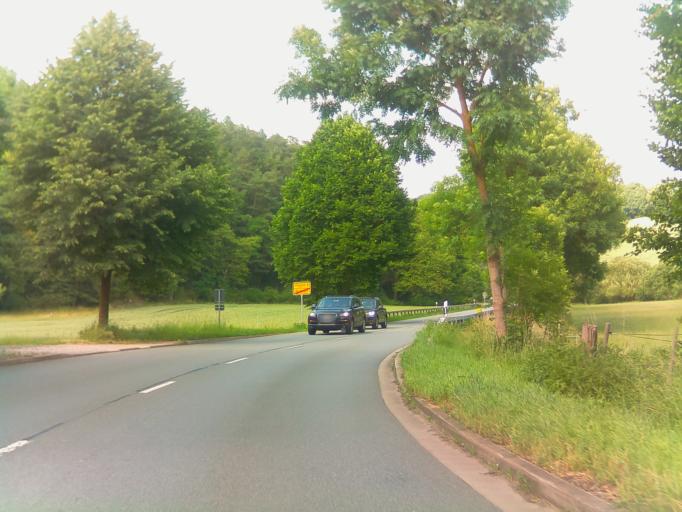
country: DE
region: Hesse
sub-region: Regierungsbezirk Kassel
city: Waldeck
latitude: 51.1889
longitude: 9.0844
